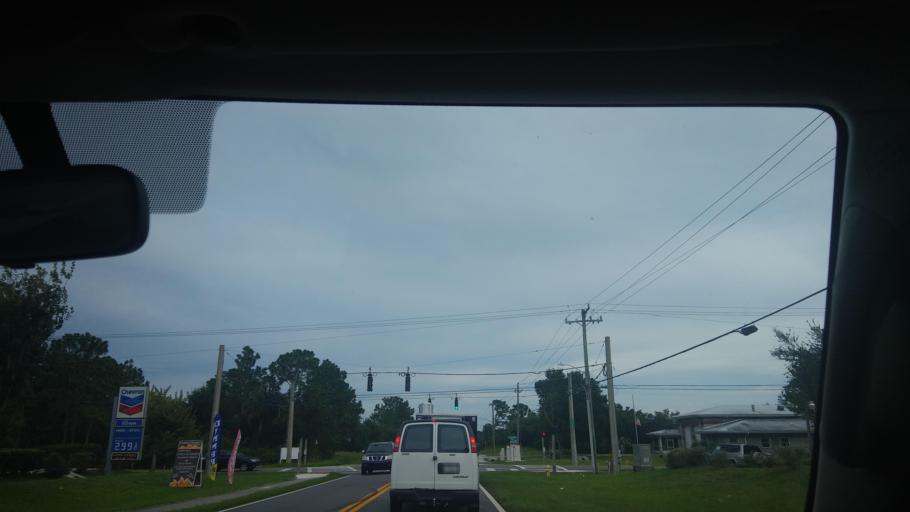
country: US
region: Florida
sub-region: Brevard County
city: Grant-Valkaria
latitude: 27.9530
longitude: -80.6287
